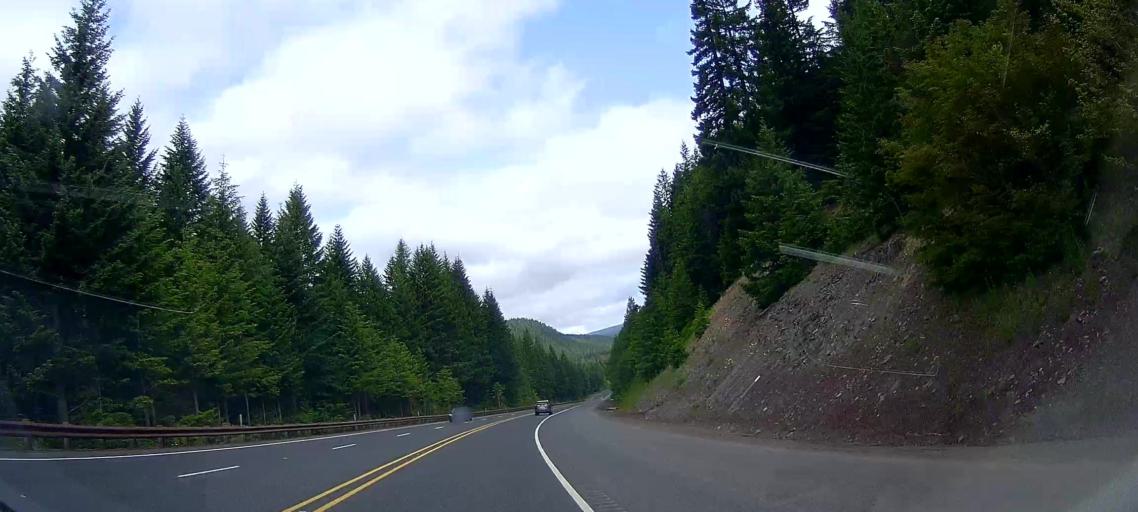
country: US
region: Oregon
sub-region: Clackamas County
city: Mount Hood Village
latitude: 45.2427
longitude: -121.7066
